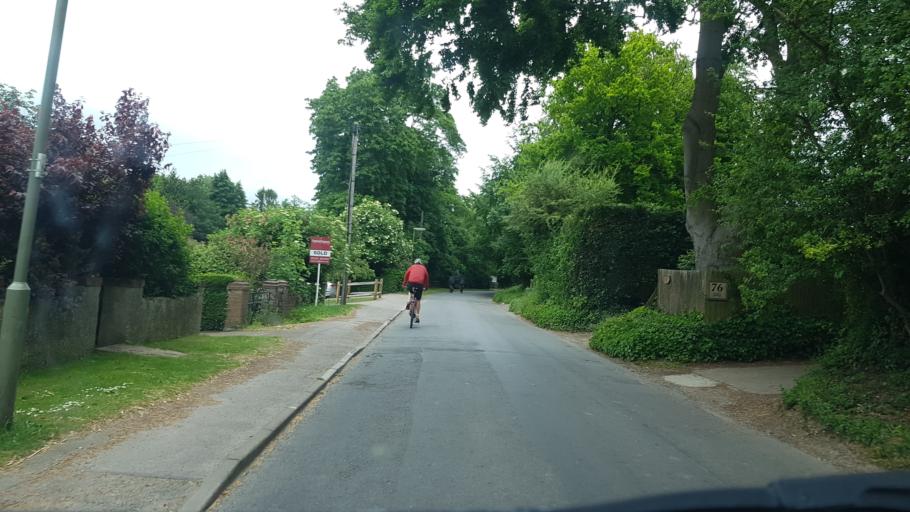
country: GB
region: England
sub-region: Surrey
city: Great Bookham
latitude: 51.2727
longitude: -0.3677
